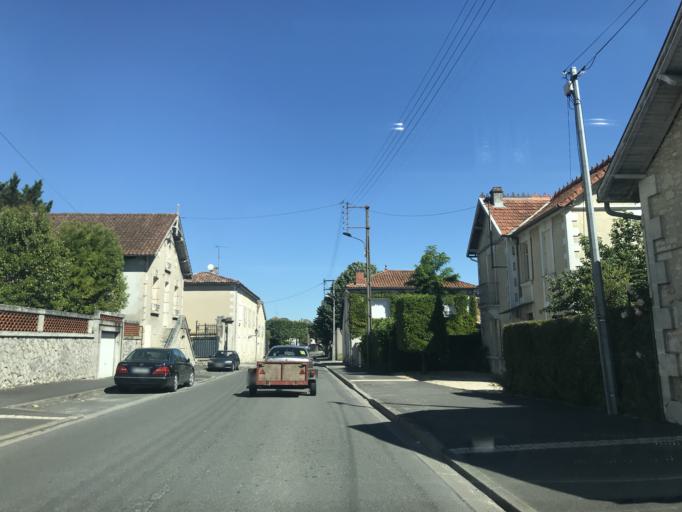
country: FR
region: Poitou-Charentes
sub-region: Departement de la Charente
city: Barbezieux-Saint-Hilaire
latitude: 45.4695
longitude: -0.1517
